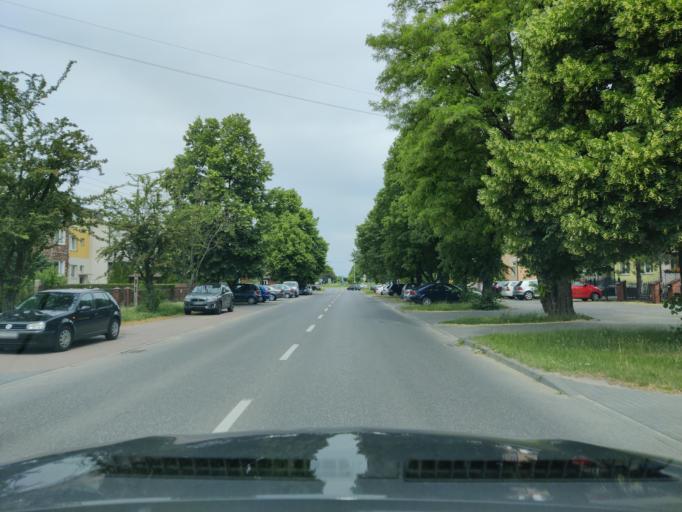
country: PL
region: Masovian Voivodeship
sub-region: Powiat wyszkowski
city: Wyszkow
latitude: 52.6043
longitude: 21.4552
